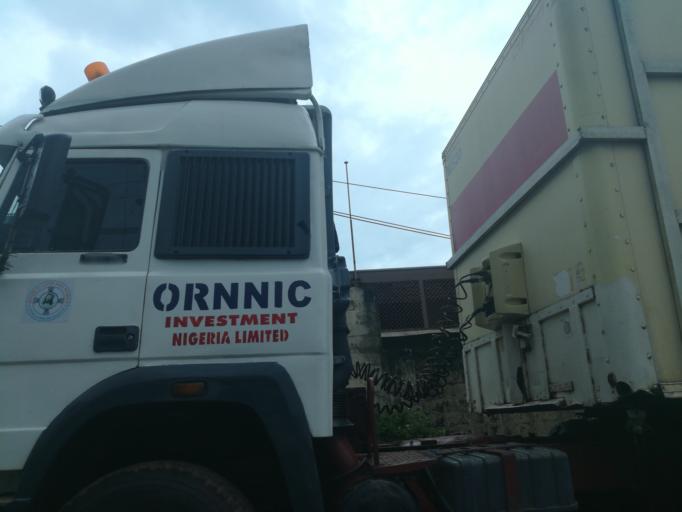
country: NG
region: Lagos
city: Agege
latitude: 6.6176
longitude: 3.3406
